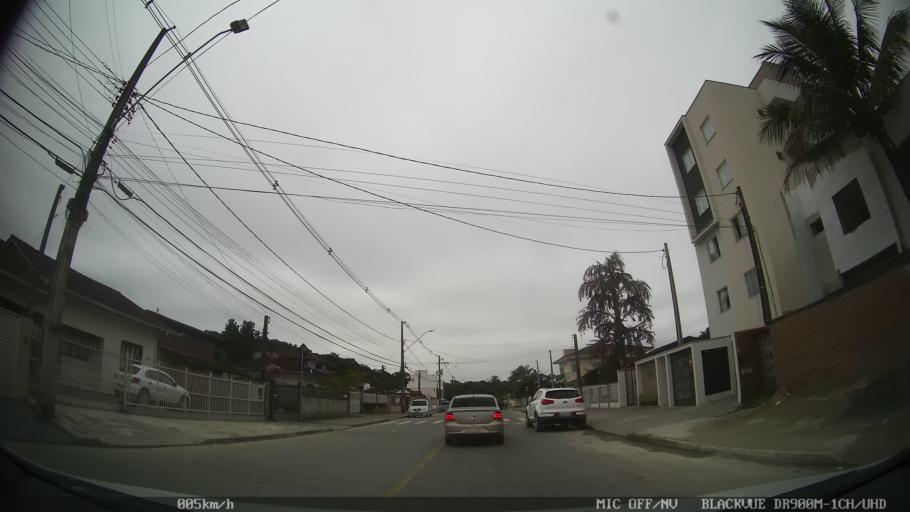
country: BR
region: Santa Catarina
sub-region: Joinville
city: Joinville
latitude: -26.2773
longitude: -48.9024
